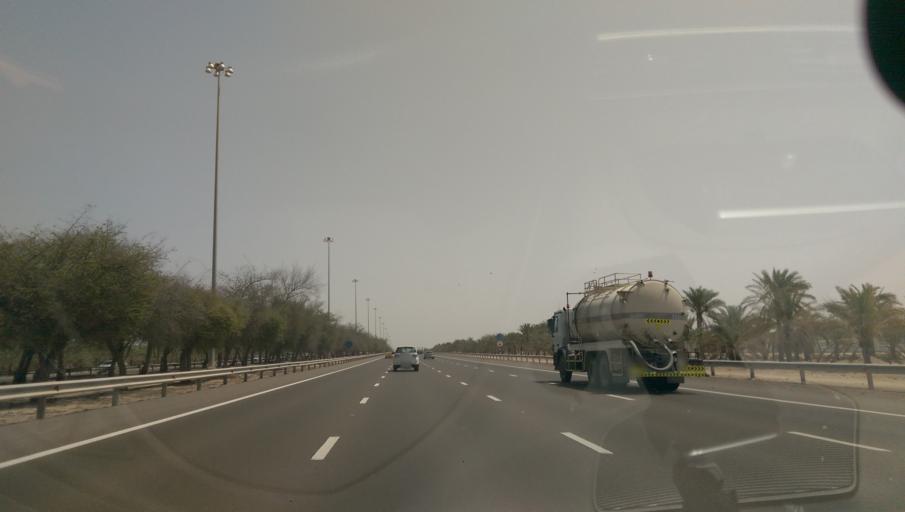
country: AE
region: Abu Dhabi
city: Abu Dhabi
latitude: 24.4954
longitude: 54.6797
